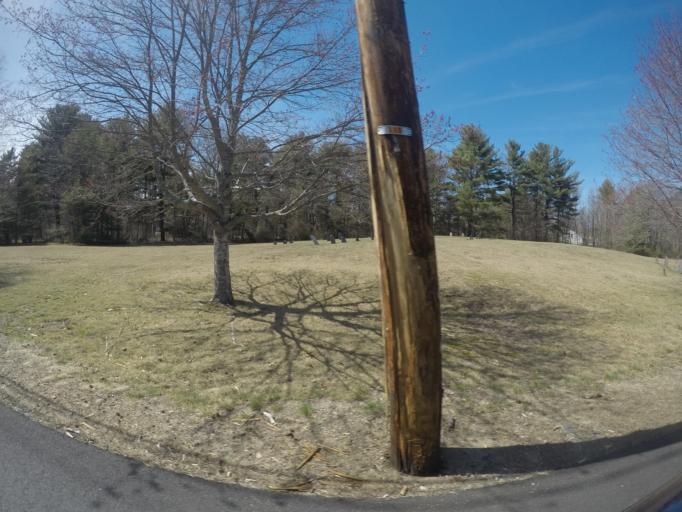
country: US
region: Massachusetts
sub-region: Bristol County
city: Easton
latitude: 42.0391
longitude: -71.0822
